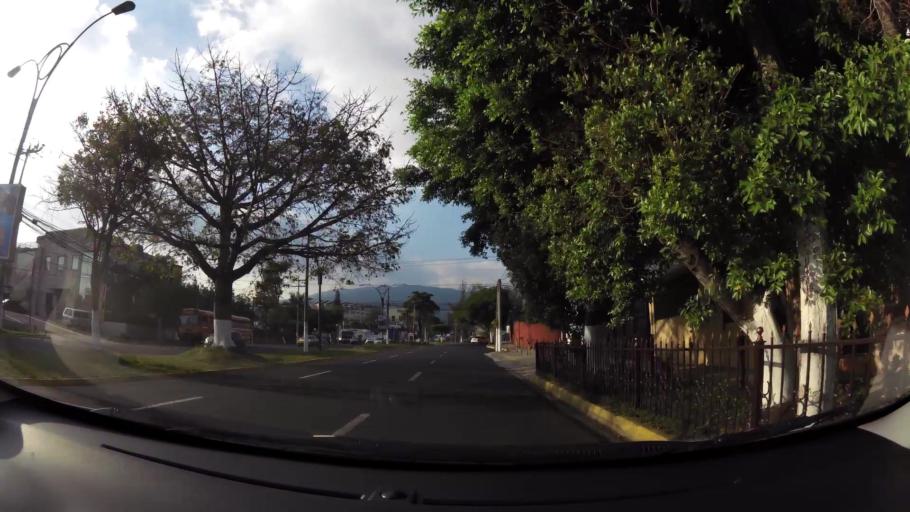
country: SV
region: La Libertad
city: Antiguo Cuscatlan
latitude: 13.6889
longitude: -89.2392
